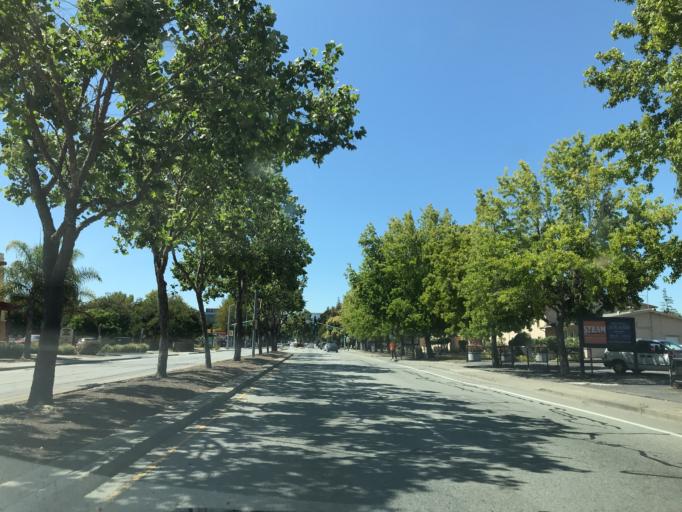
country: US
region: California
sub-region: San Mateo County
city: East Palo Alto
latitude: 37.4670
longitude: -122.1415
